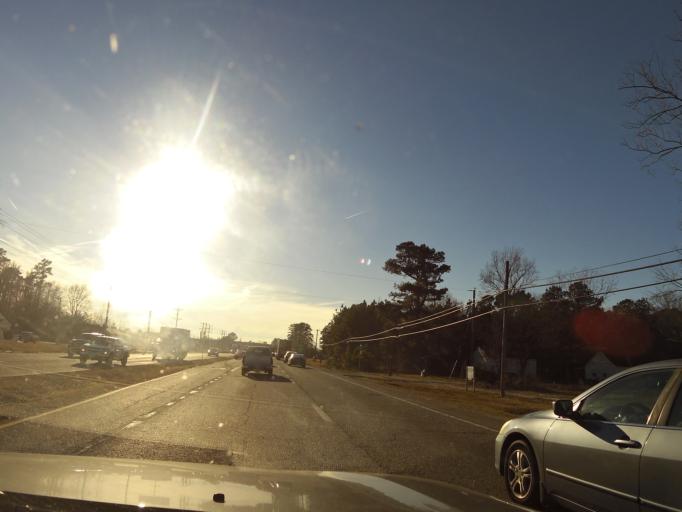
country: US
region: Virginia
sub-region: City of Suffolk
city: South Suffolk
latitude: 36.7168
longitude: -76.6599
